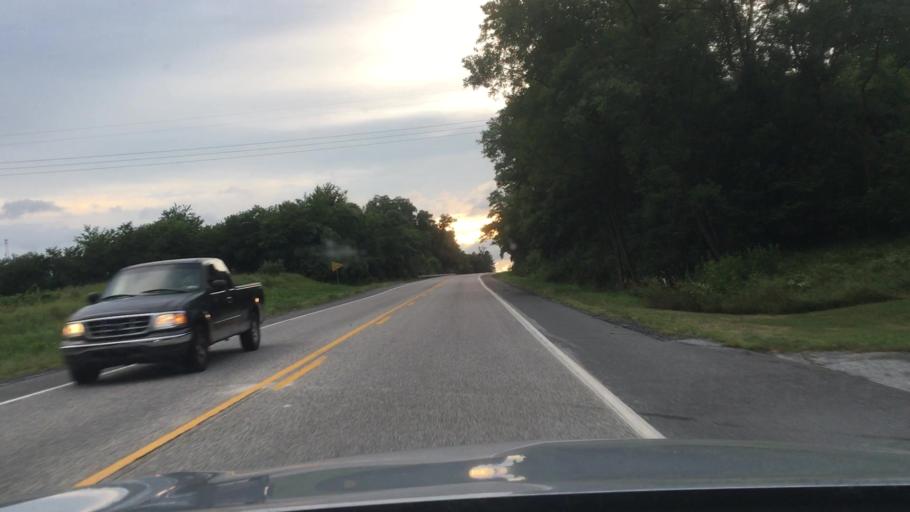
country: US
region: Pennsylvania
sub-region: York County
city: Dillsburg
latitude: 40.0959
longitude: -76.9656
